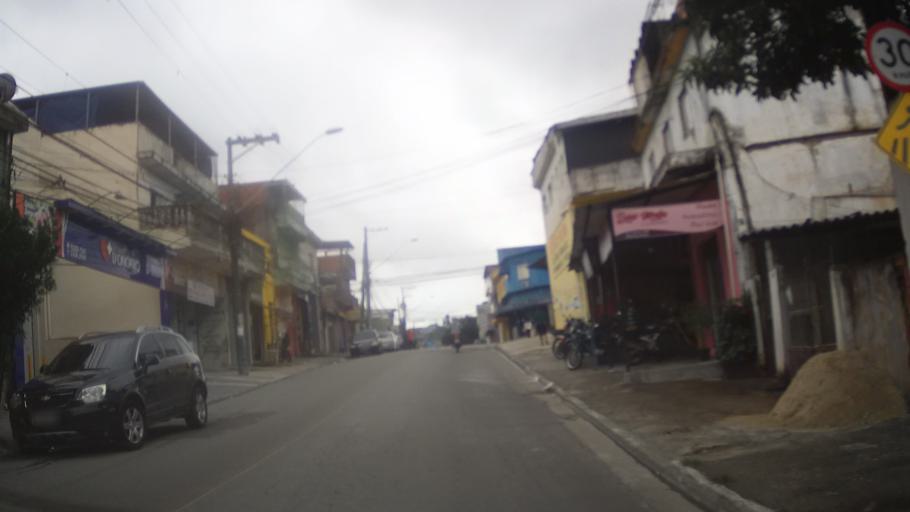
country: BR
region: Sao Paulo
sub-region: Guarulhos
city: Guarulhos
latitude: -23.4252
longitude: -46.5331
